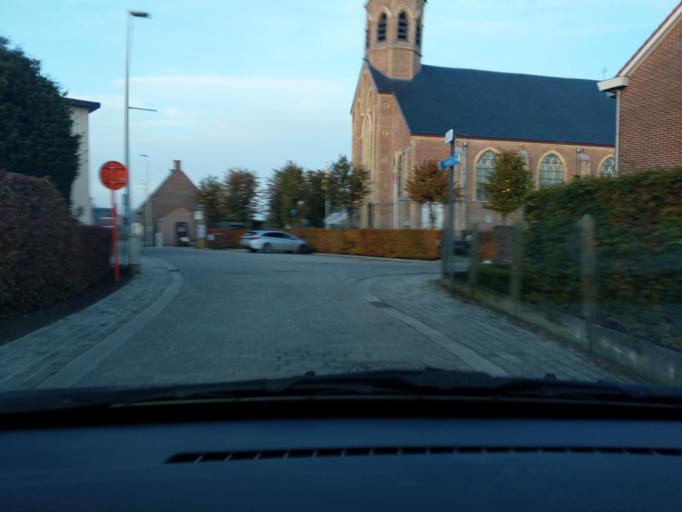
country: BE
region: Flanders
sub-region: Provincie Oost-Vlaanderen
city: Nevele
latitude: 51.0336
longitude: 3.5162
